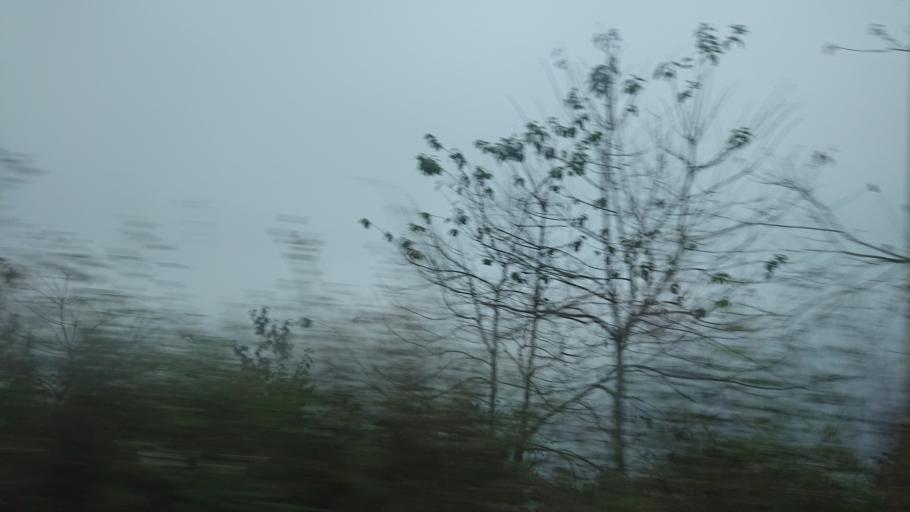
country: TW
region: Taiwan
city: Lugu
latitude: 23.5934
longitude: 120.7132
